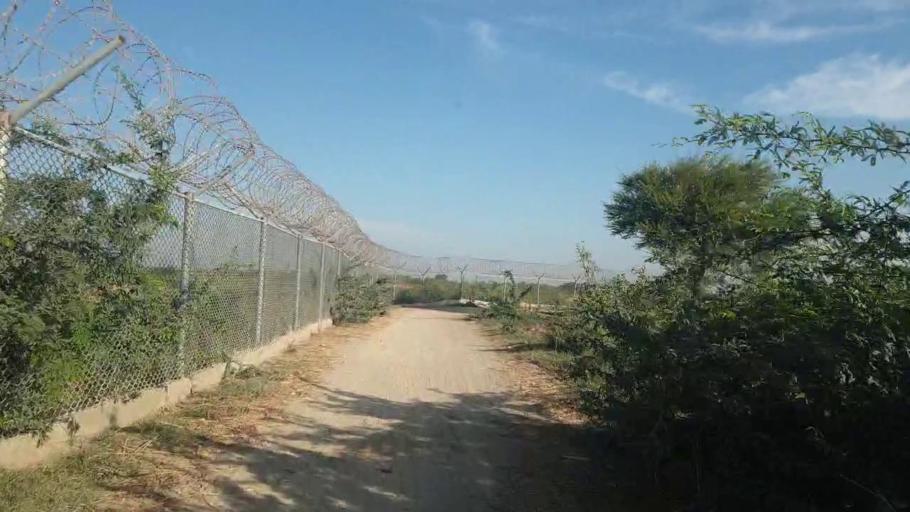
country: PK
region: Sindh
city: Talhar
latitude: 24.8486
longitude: 68.8570
